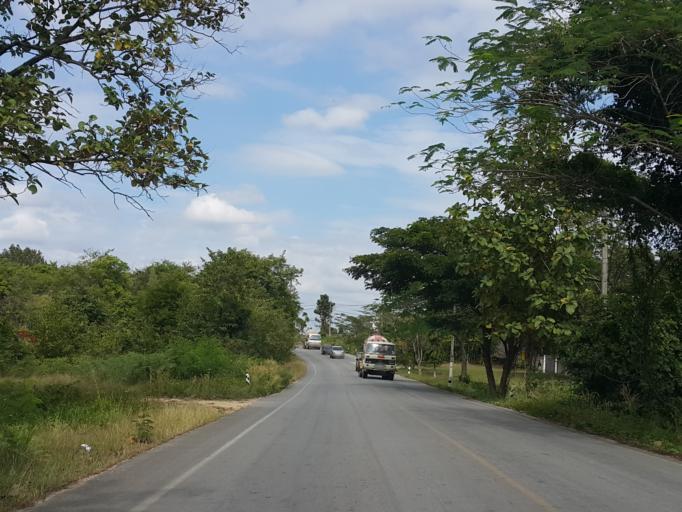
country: TH
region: Lampang
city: Lampang
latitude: 18.4082
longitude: 99.4528
